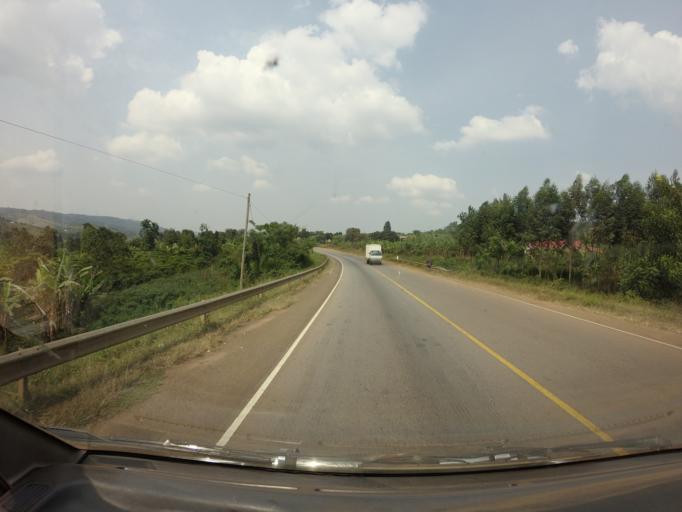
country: UG
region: Central Region
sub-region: Lwengo District
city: Lwengo
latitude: -0.3809
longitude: 31.2897
